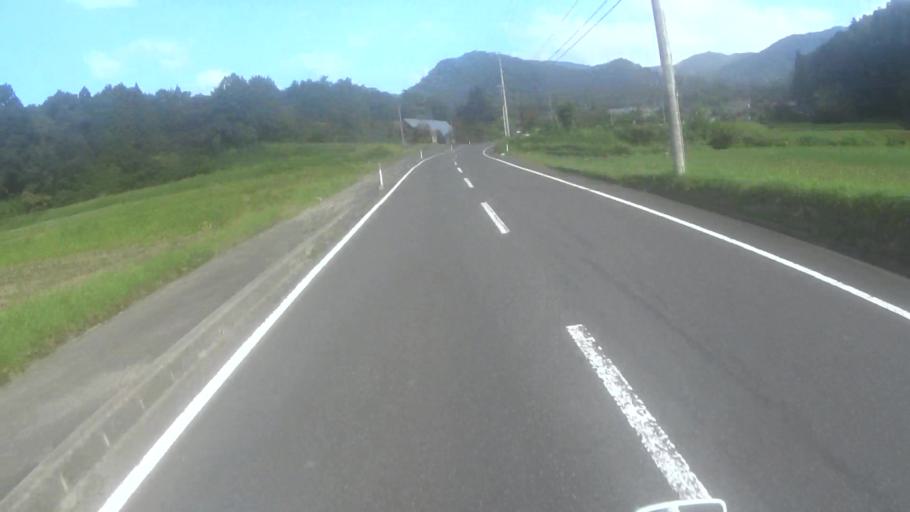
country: JP
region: Kyoto
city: Miyazu
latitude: 35.6053
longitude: 135.1468
